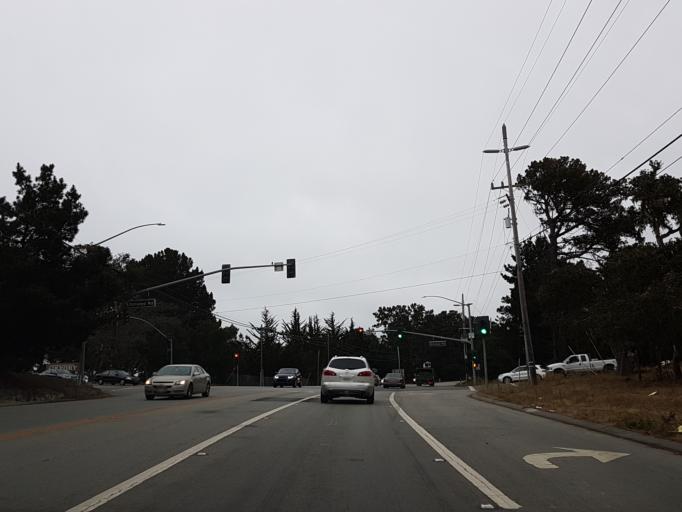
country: US
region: California
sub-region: Monterey County
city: Del Rey Oaks
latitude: 36.5839
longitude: -121.8506
